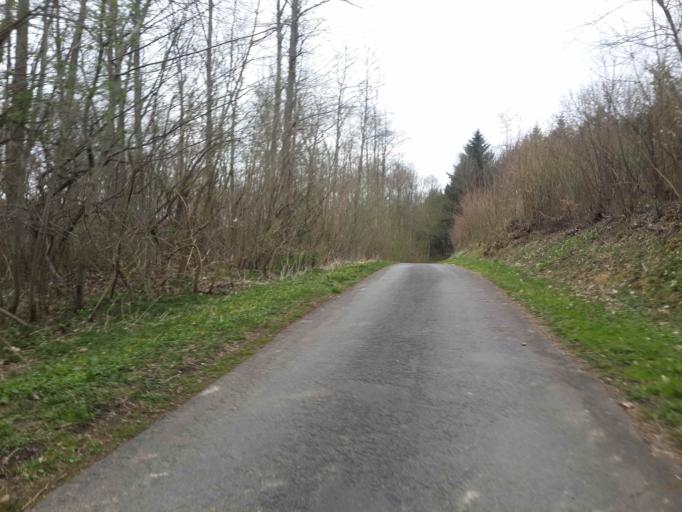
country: DE
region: Baden-Wuerttemberg
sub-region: Karlsruhe Region
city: Adelsheim
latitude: 49.4135
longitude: 9.4021
